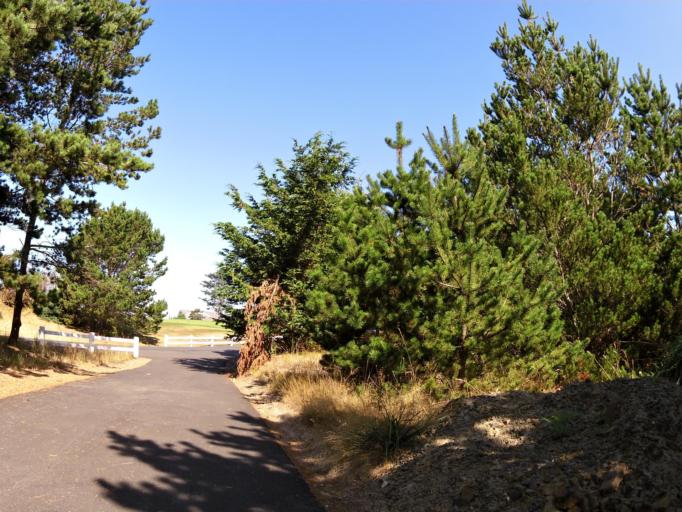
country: US
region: Oregon
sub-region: Clatsop County
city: Gearhart
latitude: 46.0472
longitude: -123.9247
